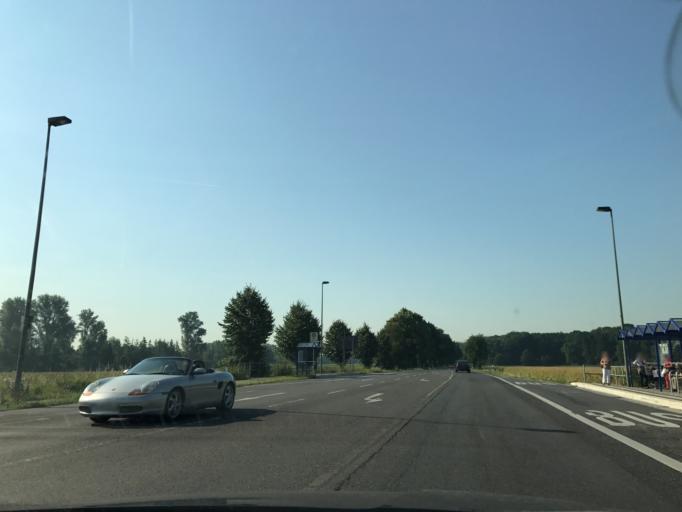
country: DE
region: North Rhine-Westphalia
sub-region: Regierungsbezirk Dusseldorf
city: Meerbusch
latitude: 51.2789
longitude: 6.6615
